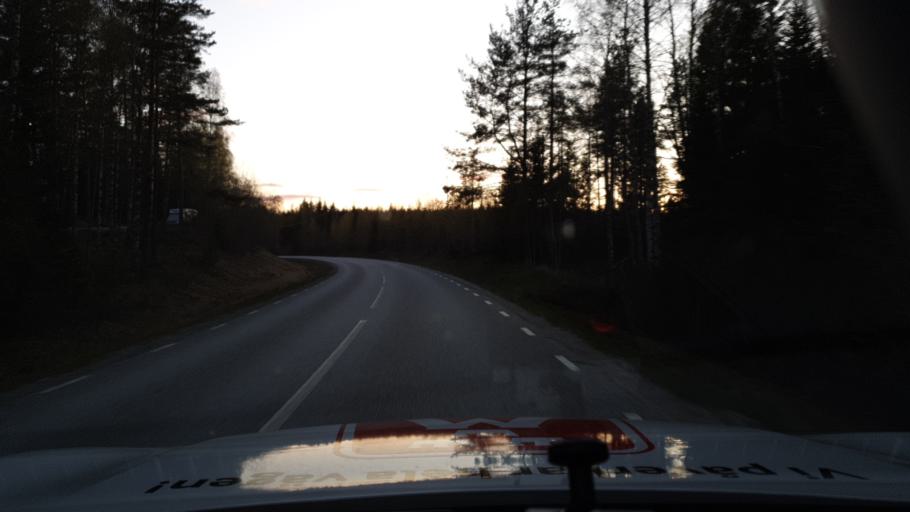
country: SE
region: Dalarna
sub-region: Smedjebackens Kommun
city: Smedjebacken
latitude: 59.9034
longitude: 15.3548
